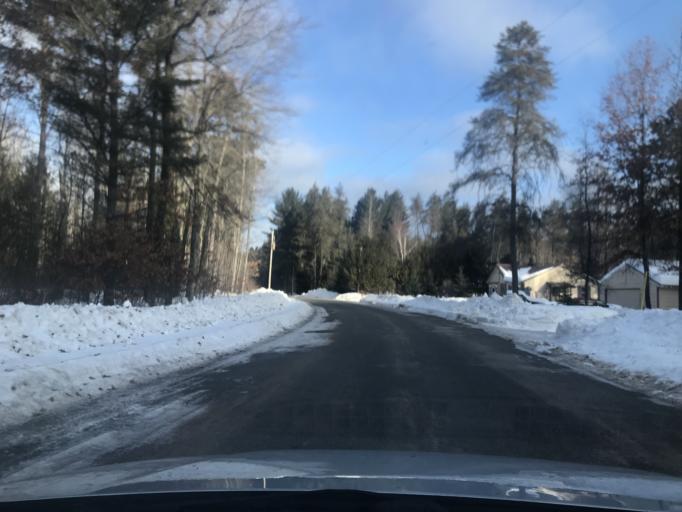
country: US
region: Wisconsin
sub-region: Marinette County
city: Niagara
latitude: 45.6327
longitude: -87.9679
